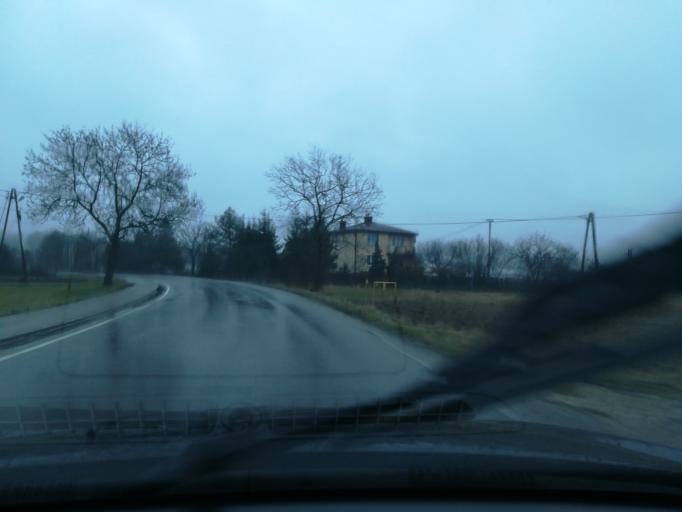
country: PL
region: Subcarpathian Voivodeship
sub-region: Powiat lancucki
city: Bialobrzegi
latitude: 50.1166
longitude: 22.3395
